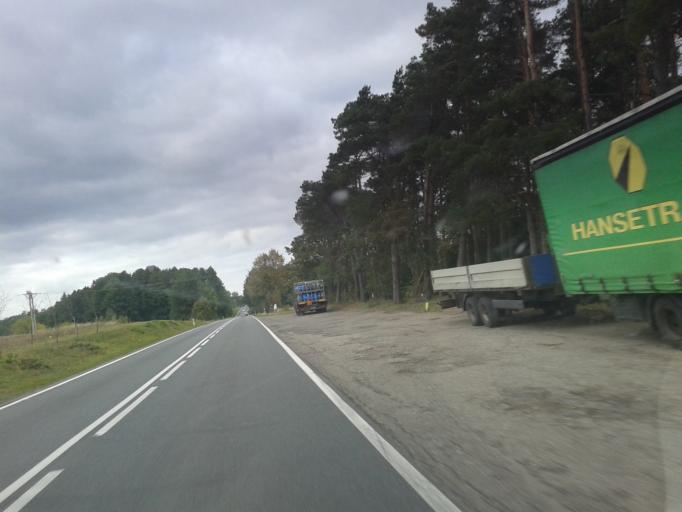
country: PL
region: Kujawsko-Pomorskie
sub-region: Powiat sepolenski
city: Sepolno Krajenskie
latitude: 53.4725
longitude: 17.5261
